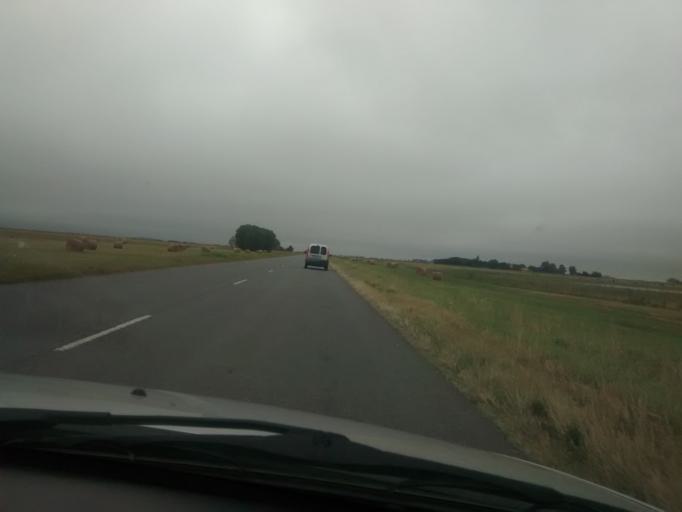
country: AR
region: Buenos Aires
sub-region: Partido de Ayacucho
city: Ayacucho
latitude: -37.2530
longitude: -58.4854
